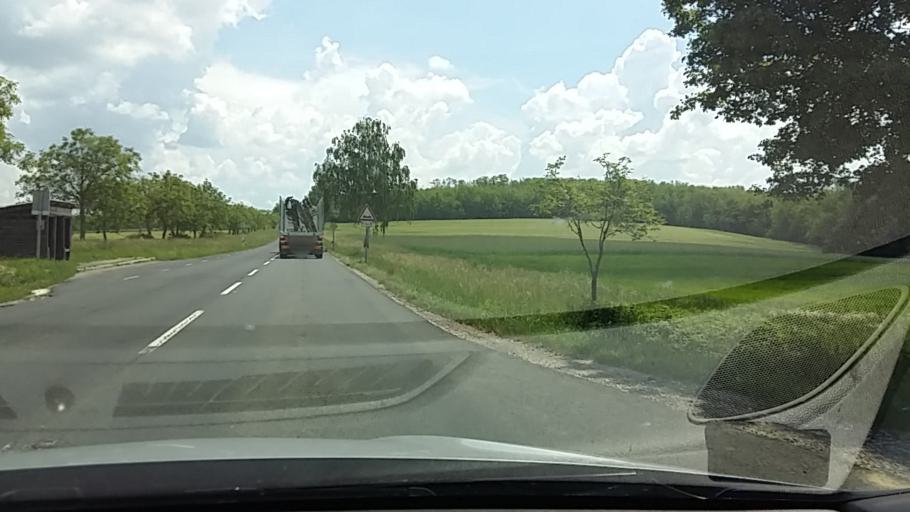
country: HU
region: Vas
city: Kormend
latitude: 46.9303
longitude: 16.6859
